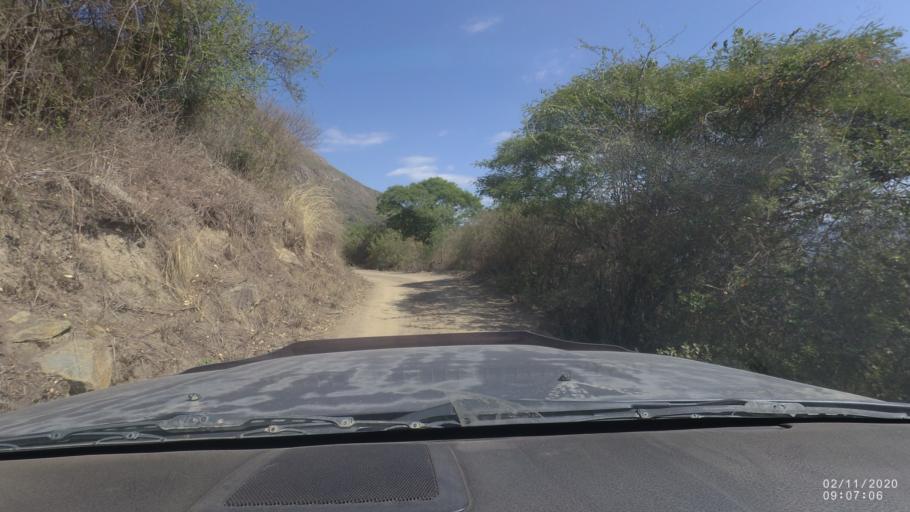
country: BO
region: Chuquisaca
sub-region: Provincia Zudanez
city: Mojocoya
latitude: -18.5316
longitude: -64.5598
